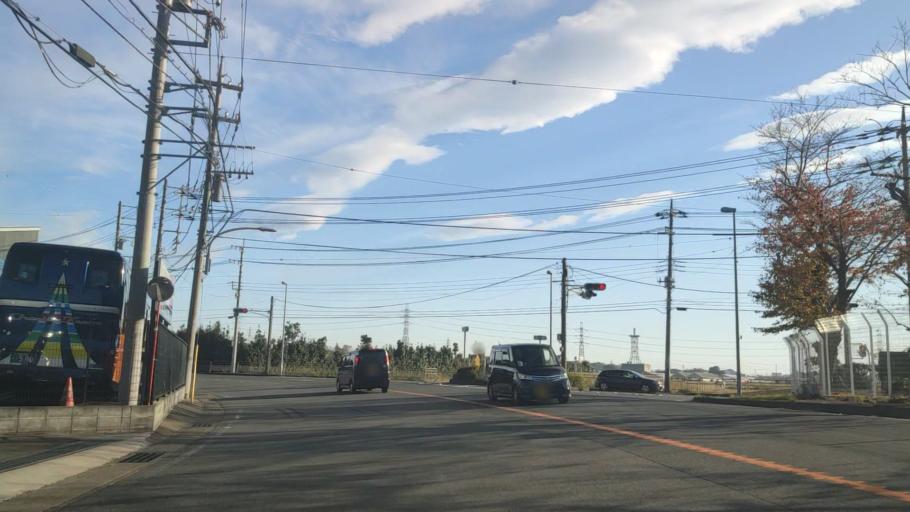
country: JP
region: Kanagawa
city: Atsugi
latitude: 35.4218
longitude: 139.3878
